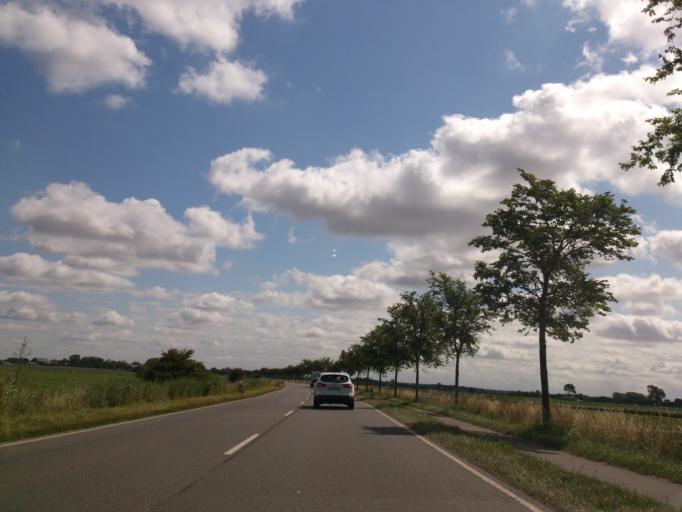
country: DE
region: Schleswig-Holstein
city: Welt
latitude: 54.2980
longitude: 8.7852
